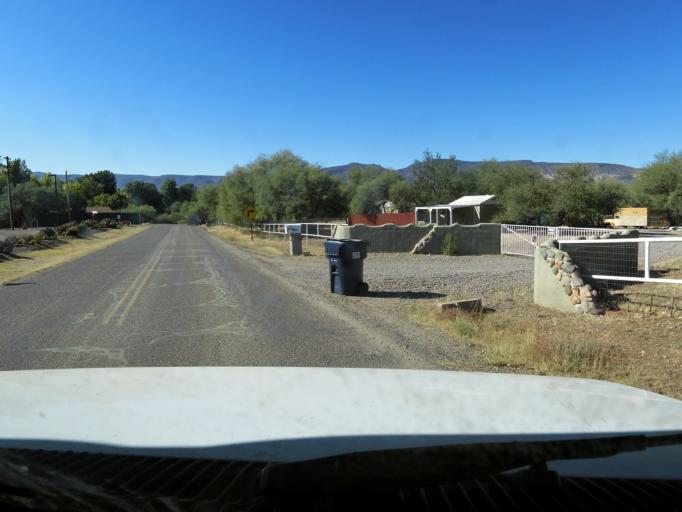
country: US
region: Arizona
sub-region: Yavapai County
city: Camp Verde
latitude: 34.5994
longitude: -111.8848
